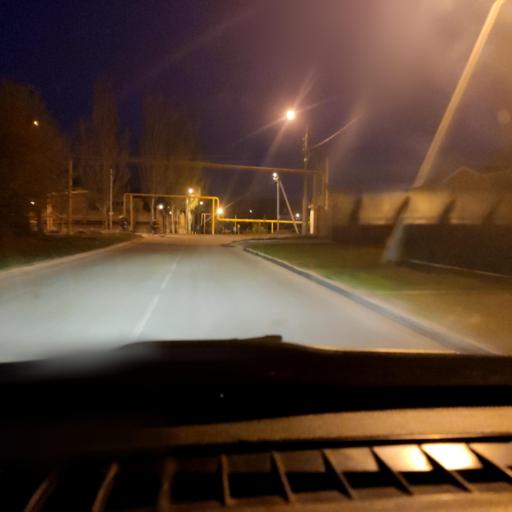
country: RU
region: Samara
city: Zhigulevsk
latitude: 53.4677
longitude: 49.6314
